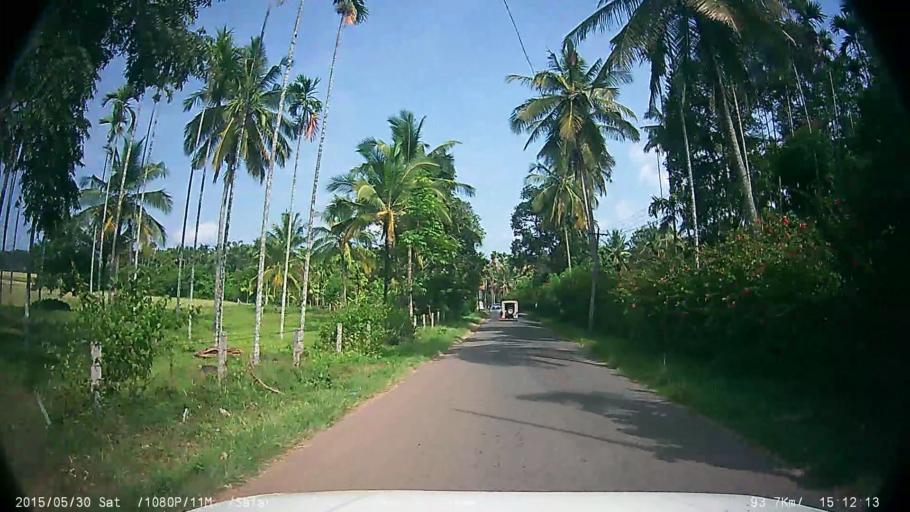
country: IN
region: Kerala
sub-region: Wayanad
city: Panamaram
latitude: 11.7975
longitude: 76.0390
